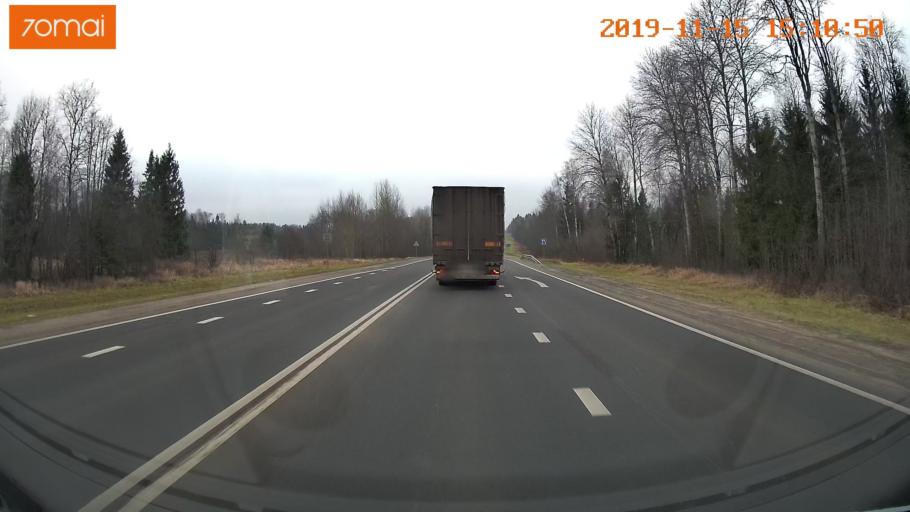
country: RU
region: Jaroslavl
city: Prechistoye
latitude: 58.3438
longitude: 40.2503
